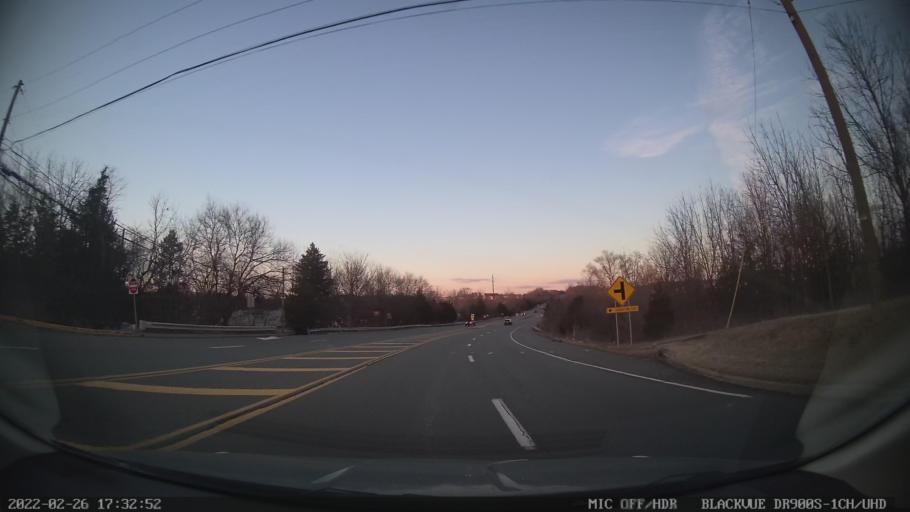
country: US
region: Pennsylvania
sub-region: Montgomery County
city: East Greenville
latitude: 40.4021
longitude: -75.4933
